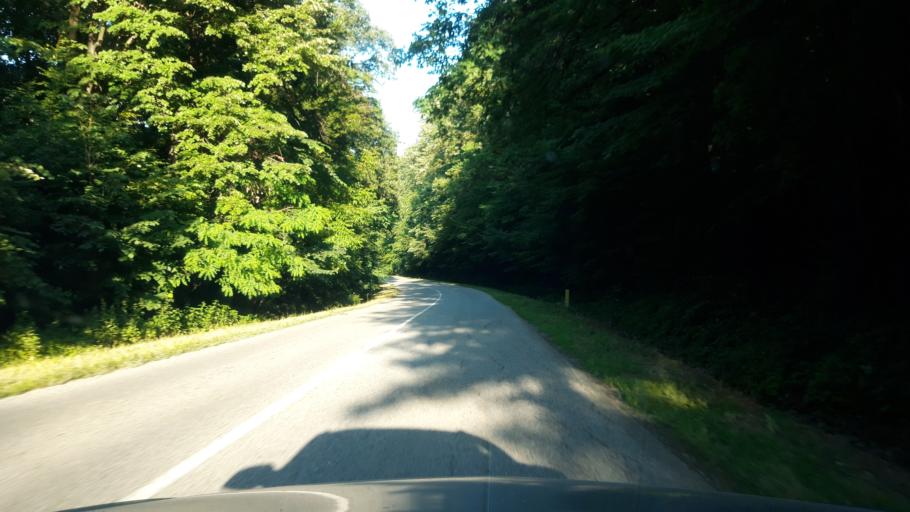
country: RS
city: Glozan
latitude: 45.1540
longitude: 19.5822
